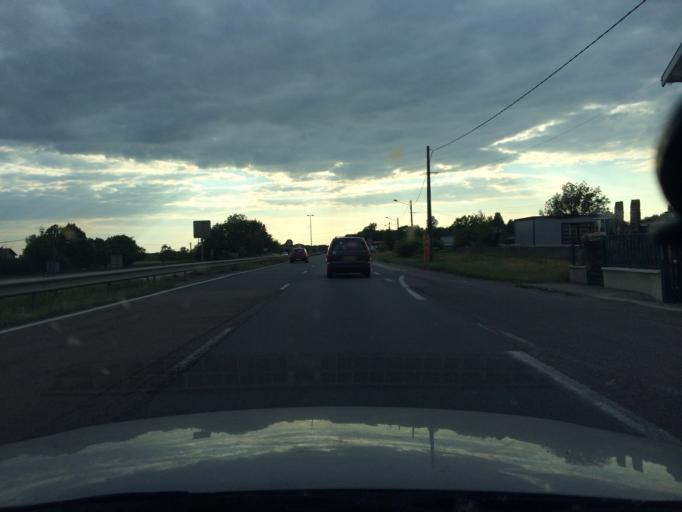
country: FR
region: Champagne-Ardenne
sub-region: Departement de la Haute-Marne
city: Villiers-en-Lieu
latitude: 48.6416
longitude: 4.9071
